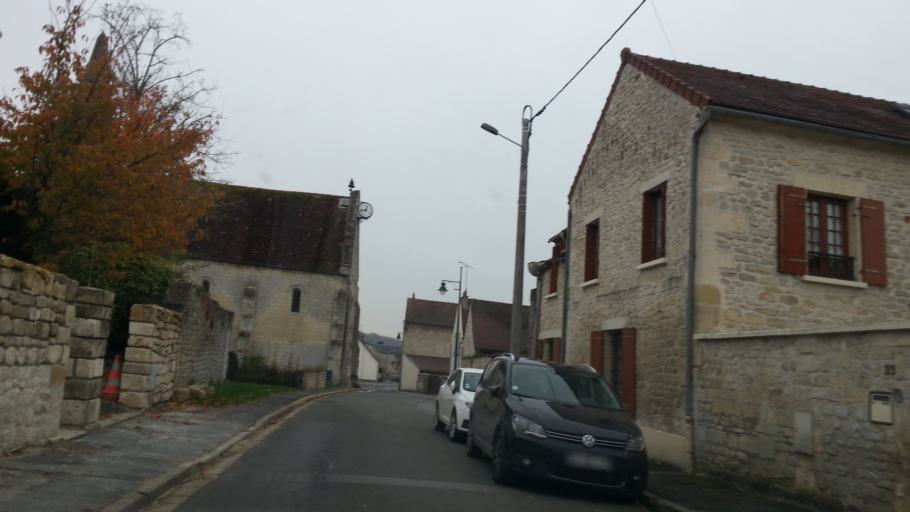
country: FR
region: Picardie
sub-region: Departement de l'Oise
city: Villers-sous-Saint-Leu
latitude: 49.2137
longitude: 2.3980
